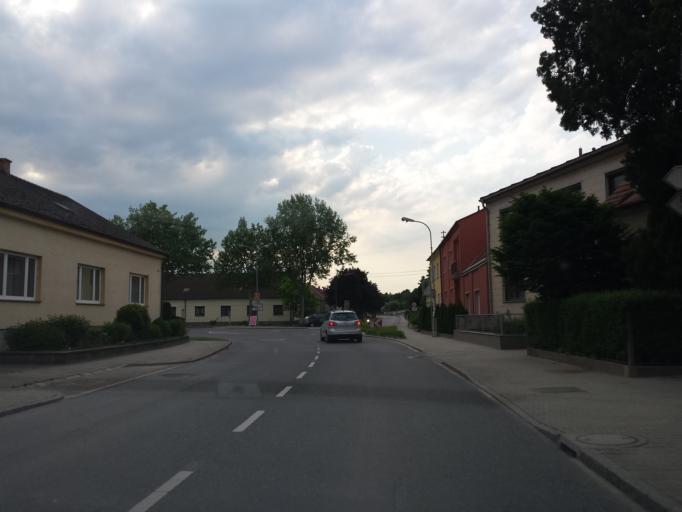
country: AT
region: Lower Austria
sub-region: Politischer Bezirk Ganserndorf
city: Markgrafneusiedl
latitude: 48.2683
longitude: 16.6304
